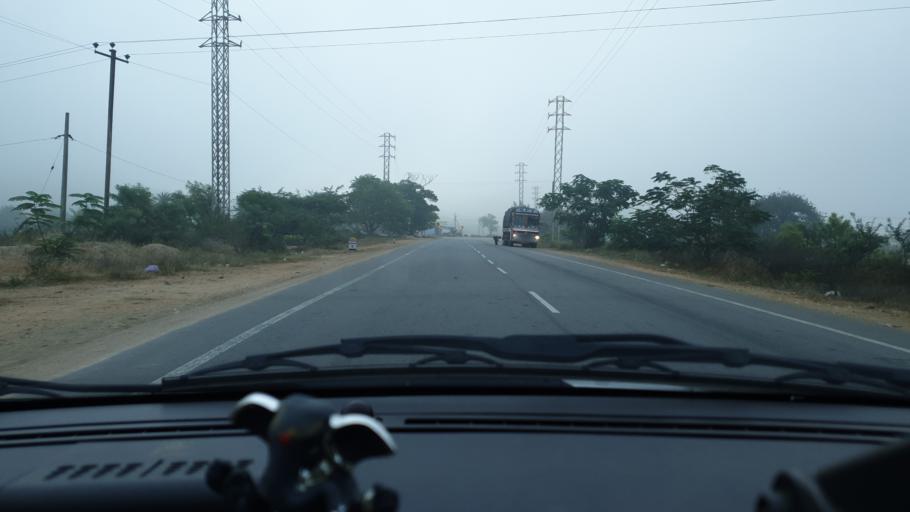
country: IN
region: Telangana
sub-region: Mahbubnagar
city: Farrukhnagar
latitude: 16.9031
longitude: 78.5303
